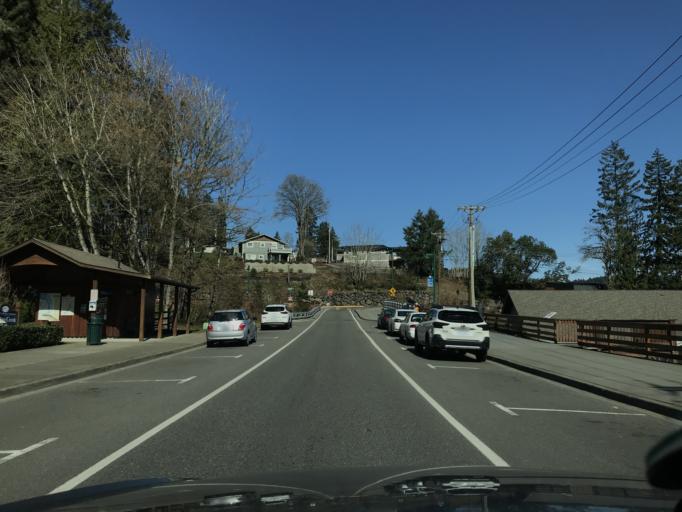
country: US
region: Washington
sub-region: Pierce County
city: Gig Harbor
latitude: 47.3373
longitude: -122.5940
